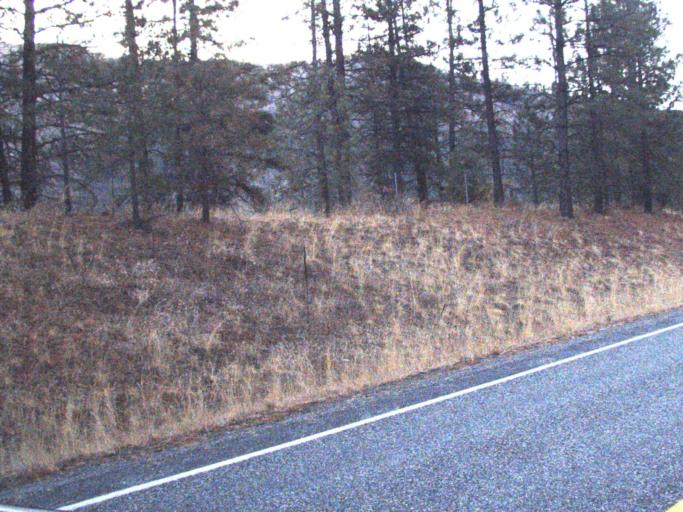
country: US
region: Washington
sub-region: Okanogan County
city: Coulee Dam
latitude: 48.1314
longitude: -118.6932
